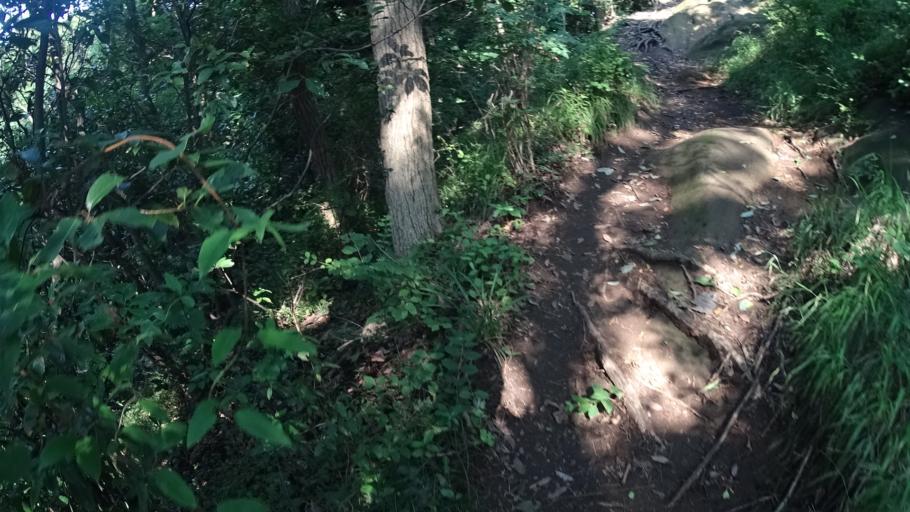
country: JP
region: Kanagawa
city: Zushi
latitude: 35.3045
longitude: 139.6144
